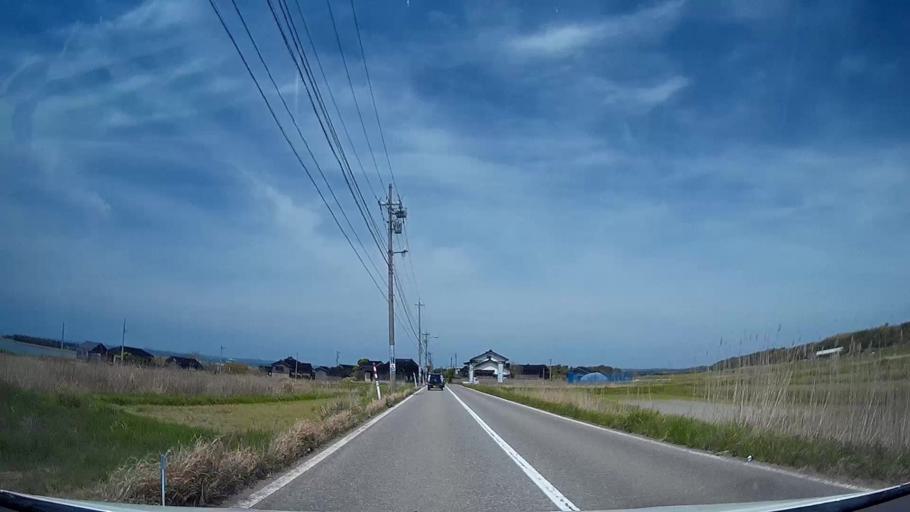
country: JP
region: Ishikawa
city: Hakui
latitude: 36.9413
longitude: 136.7615
